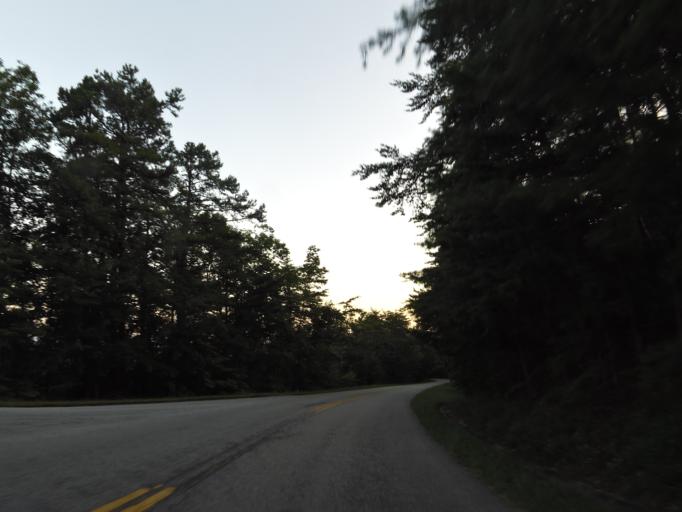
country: US
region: Tennessee
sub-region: Blount County
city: Maryville
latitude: 35.6040
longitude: -83.9815
